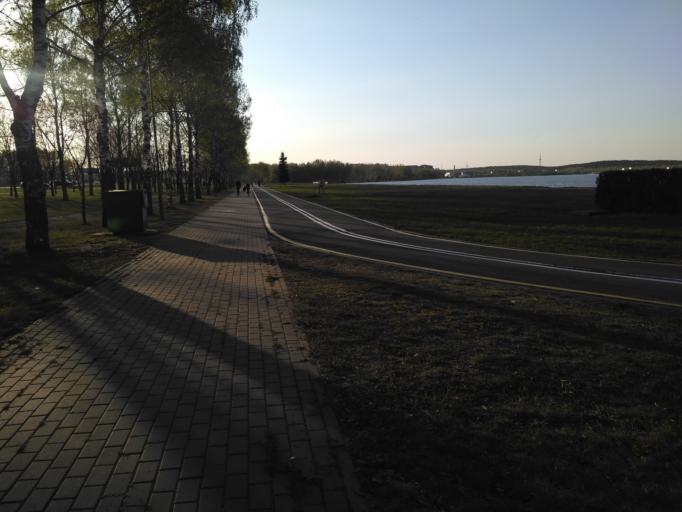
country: BY
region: Minsk
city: Zhdanovichy
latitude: 53.9433
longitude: 27.4650
